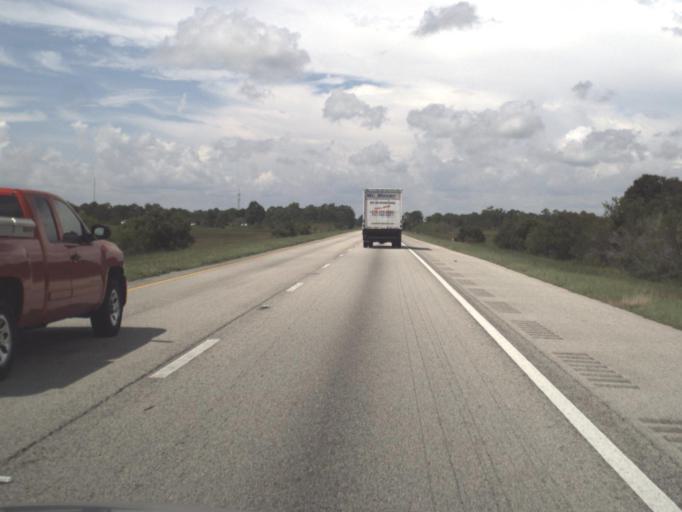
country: US
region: Florida
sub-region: Lee County
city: Suncoast Estates
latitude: 26.8014
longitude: -81.9176
